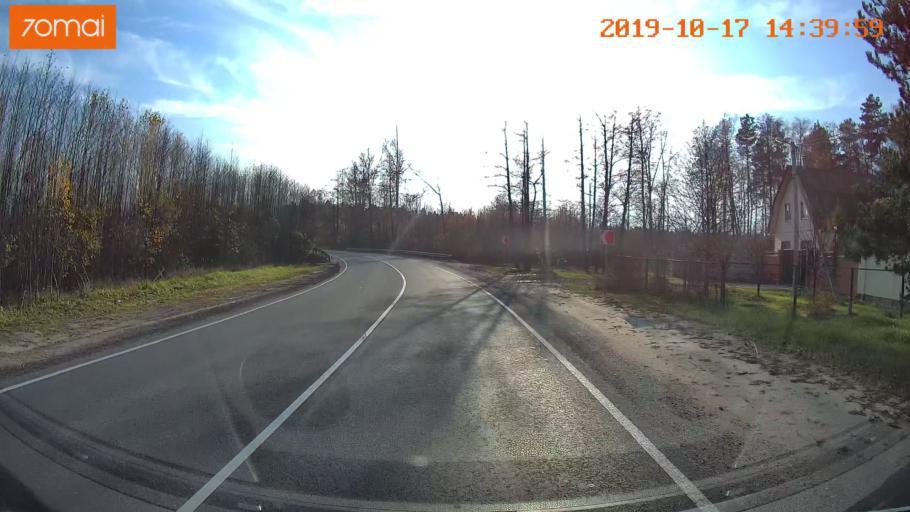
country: RU
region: Rjazan
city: Solotcha
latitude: 54.8586
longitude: 39.9623
